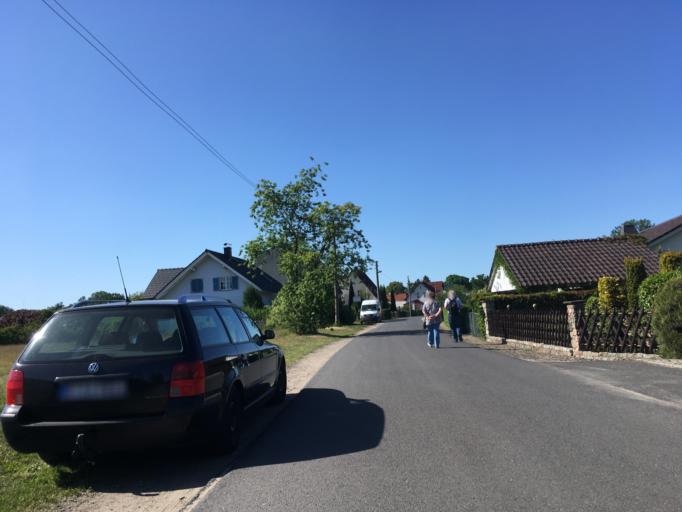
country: DE
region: Brandenburg
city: Joachimsthal
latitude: 52.9750
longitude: 13.7613
